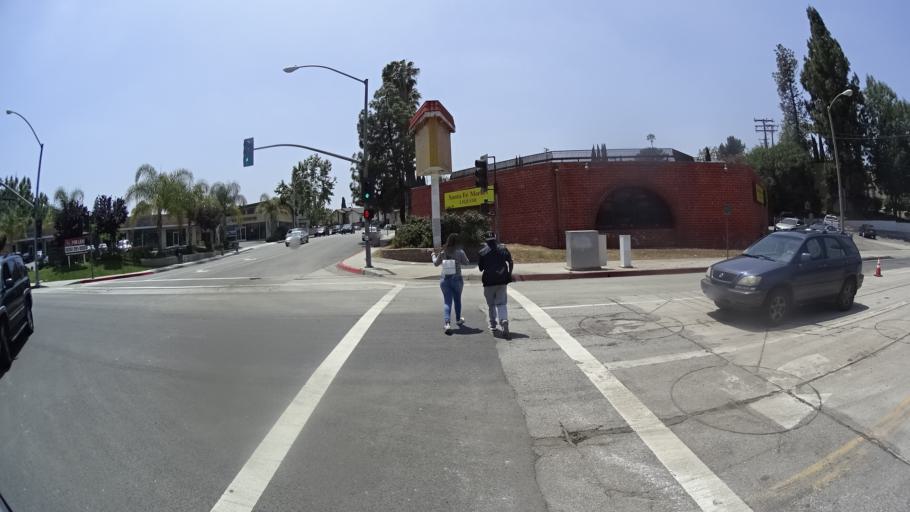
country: US
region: California
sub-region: Los Angeles County
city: Belvedere
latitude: 34.0624
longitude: -118.1529
